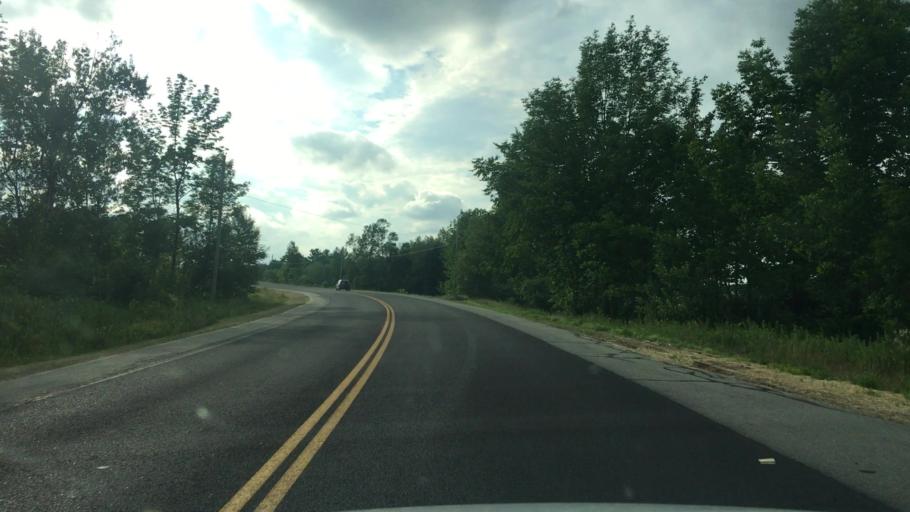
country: US
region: Maine
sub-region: Waldo County
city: Searsmont
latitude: 44.4077
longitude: -69.3054
